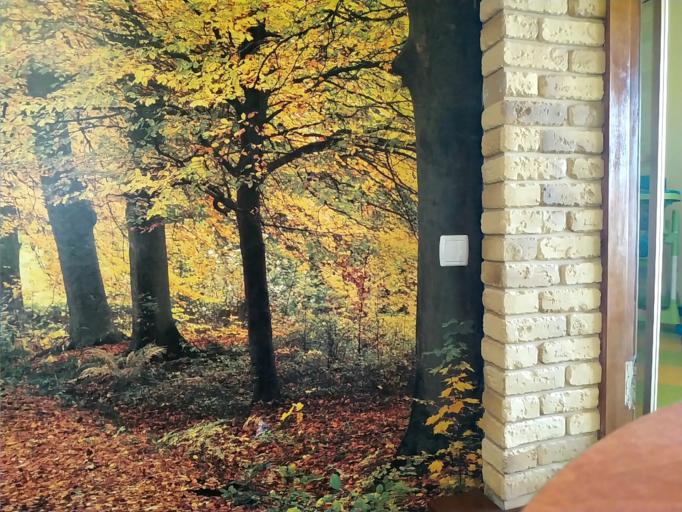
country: RU
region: Tverskaya
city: Maksatikha
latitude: 57.5848
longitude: 35.9357
